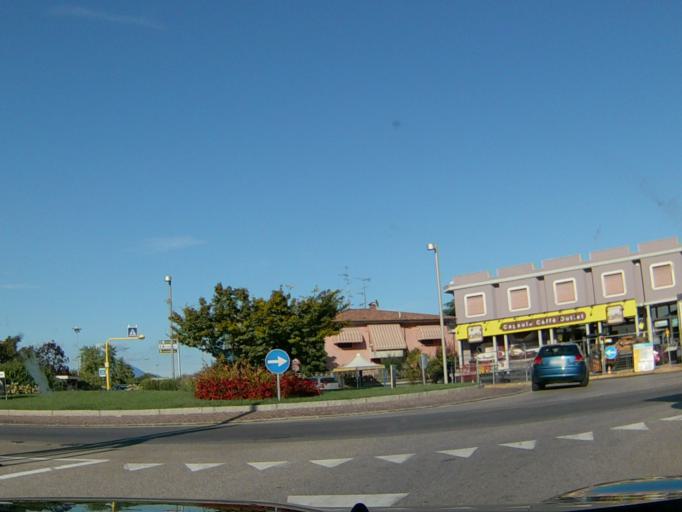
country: IT
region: Lombardy
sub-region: Provincia di Brescia
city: Molinetto
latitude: 45.4987
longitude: 10.3485
